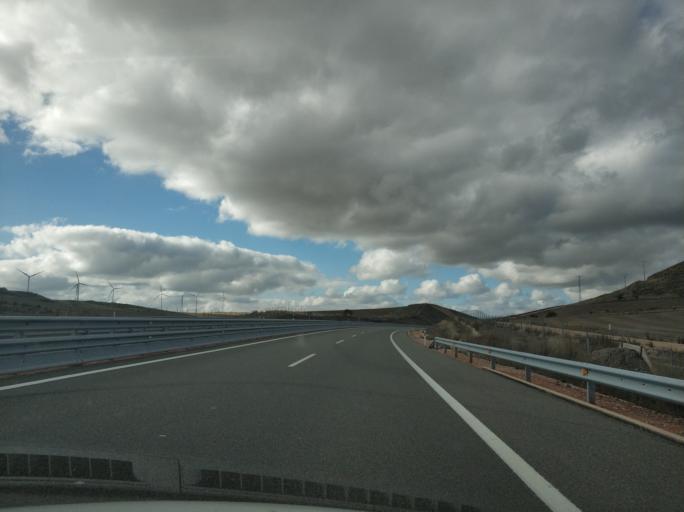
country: ES
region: Castille and Leon
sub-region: Provincia de Soria
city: Medinaceli
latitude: 41.1938
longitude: -2.4504
